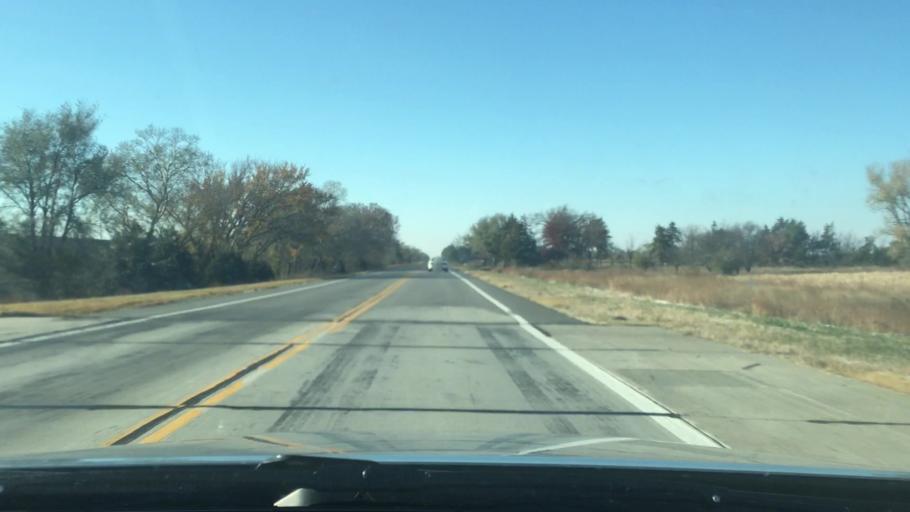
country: US
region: Kansas
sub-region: Reno County
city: Nickerson
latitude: 38.1061
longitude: -98.0233
